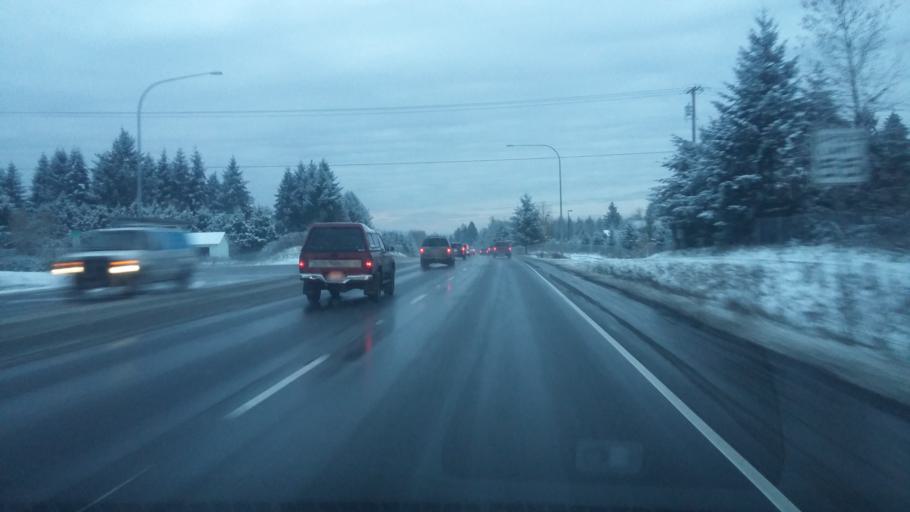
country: US
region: Washington
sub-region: Clark County
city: Brush Prairie
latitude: 45.7329
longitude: -122.5516
